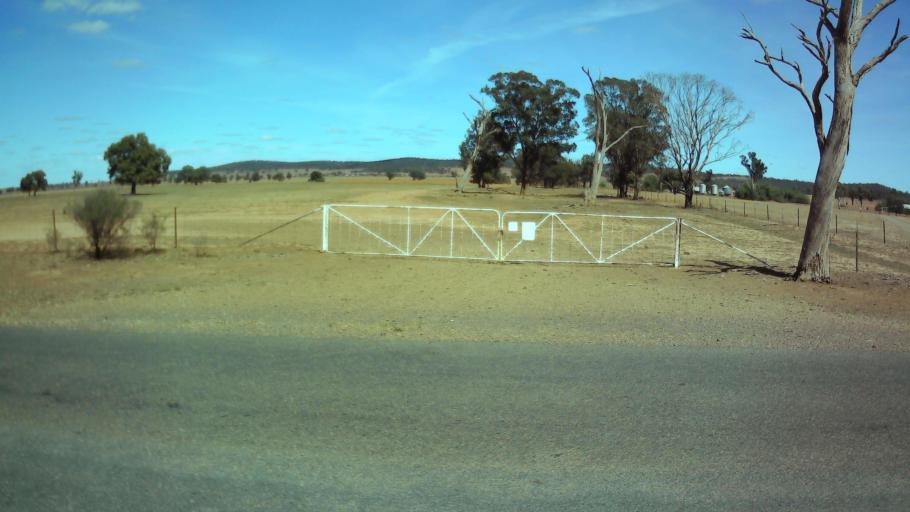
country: AU
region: New South Wales
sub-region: Forbes
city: Forbes
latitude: -33.7158
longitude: 147.8037
